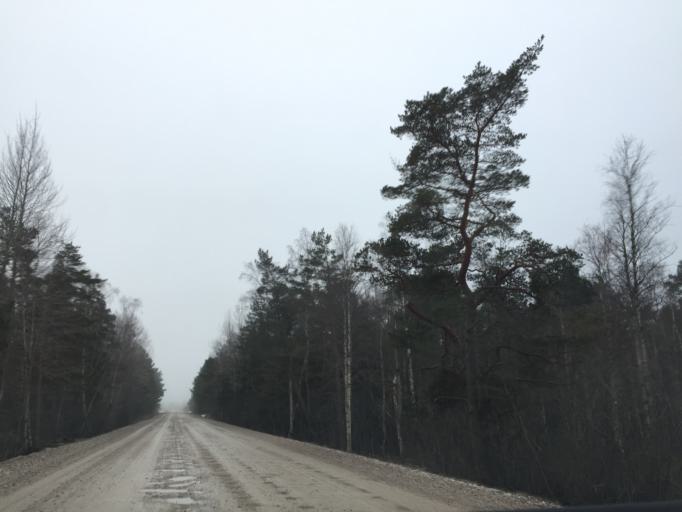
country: EE
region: Saare
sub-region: Kuressaare linn
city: Kuressaare
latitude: 58.4730
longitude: 22.0022
